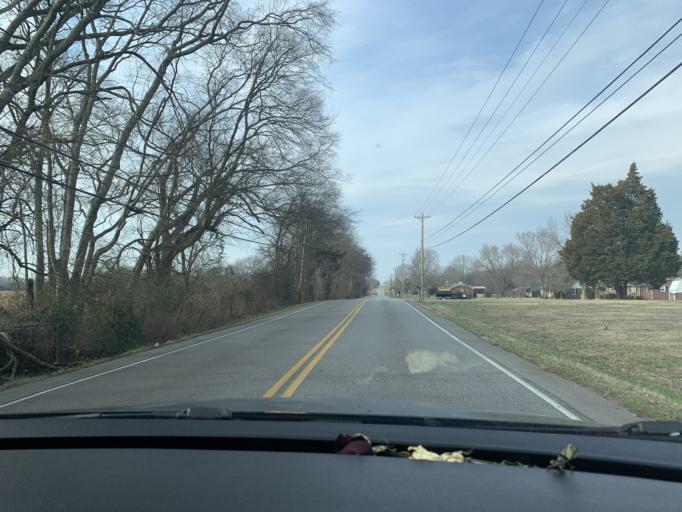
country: US
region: Tennessee
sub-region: Rutherford County
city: Smyrna
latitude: 35.9216
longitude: -86.4787
